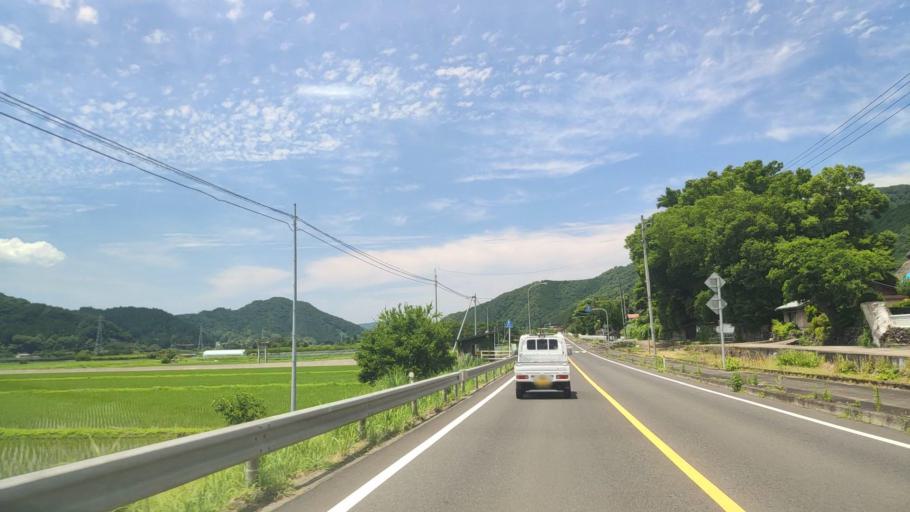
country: JP
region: Tottori
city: Tottori
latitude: 35.3681
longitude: 134.3125
